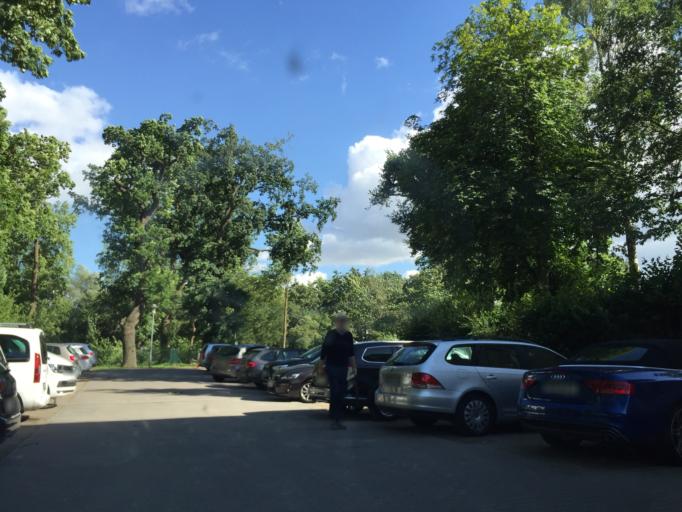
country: DE
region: Mecklenburg-Vorpommern
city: Neubrandenburg
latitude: 53.5471
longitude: 13.2520
